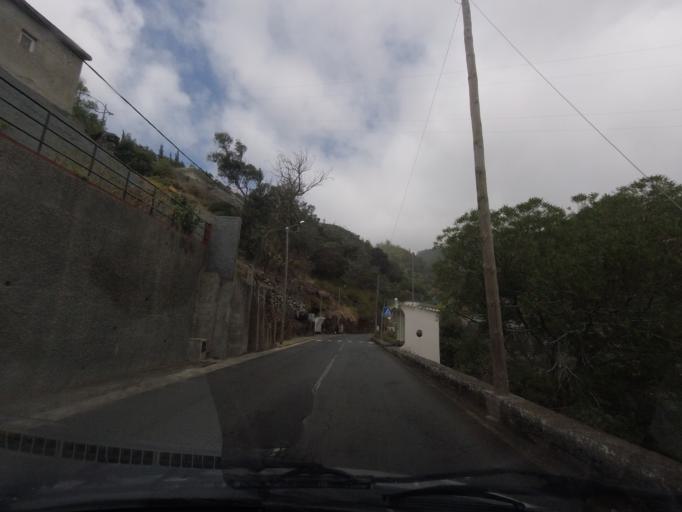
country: PT
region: Madeira
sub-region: Machico
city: Machico
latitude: 32.7058
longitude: -16.7776
